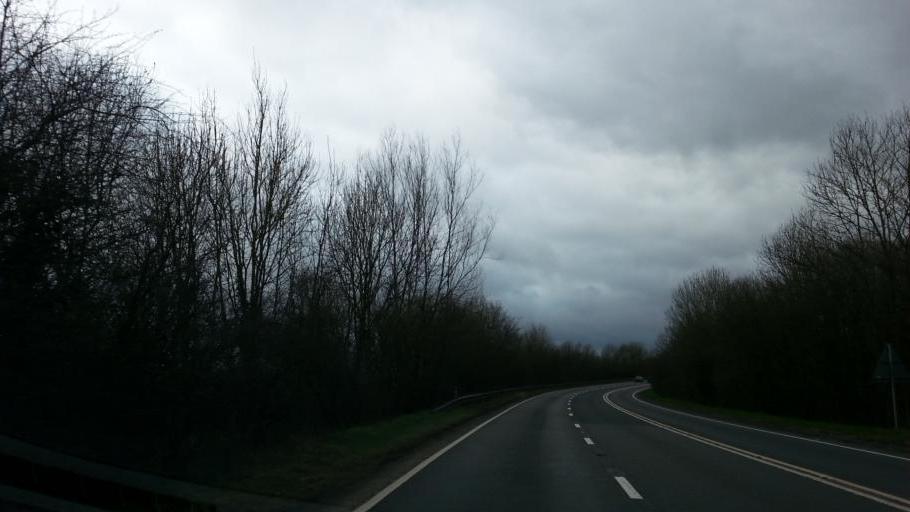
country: GB
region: England
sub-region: Devon
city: Tiverton
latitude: 50.9171
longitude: -3.5093
